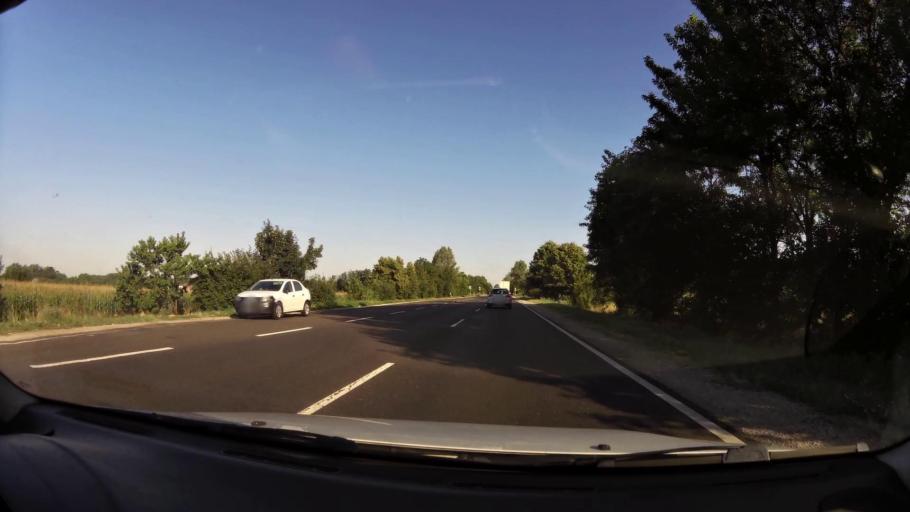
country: HU
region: Pest
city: Albertirsa
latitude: 47.2563
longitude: 19.6309
